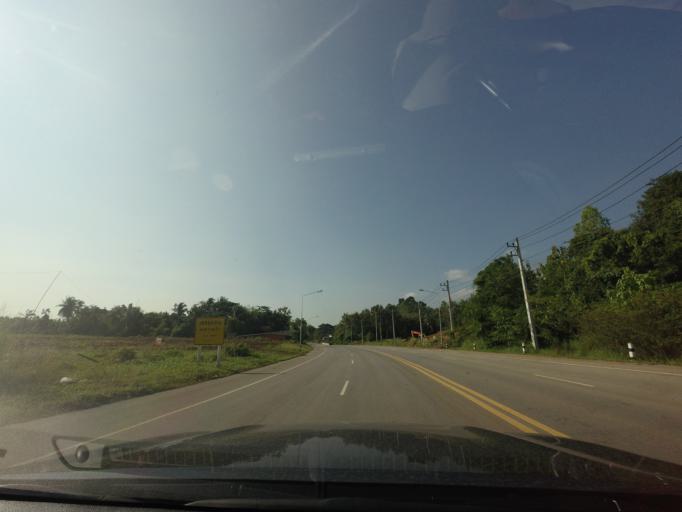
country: TH
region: Phetchabun
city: Lom Kao
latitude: 16.8699
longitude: 101.1706
